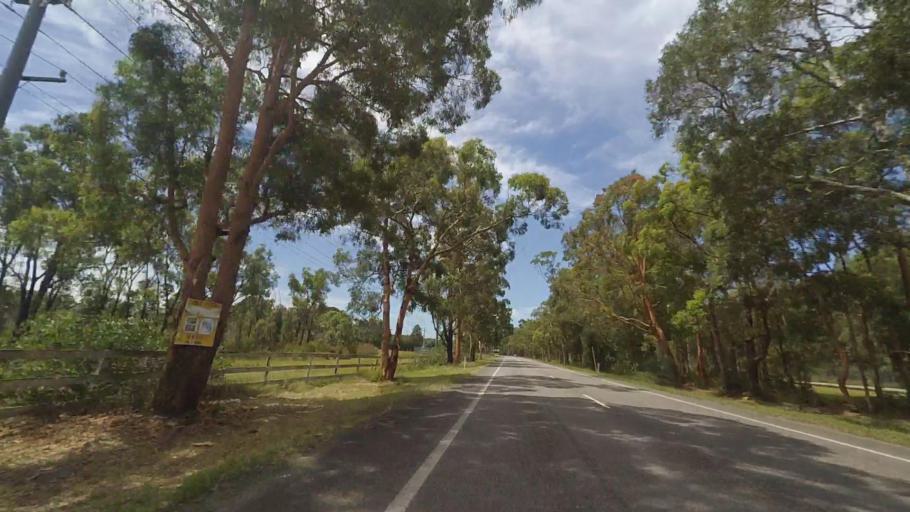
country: AU
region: New South Wales
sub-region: Port Stephens Shire
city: Medowie
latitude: -32.7680
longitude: 151.8627
